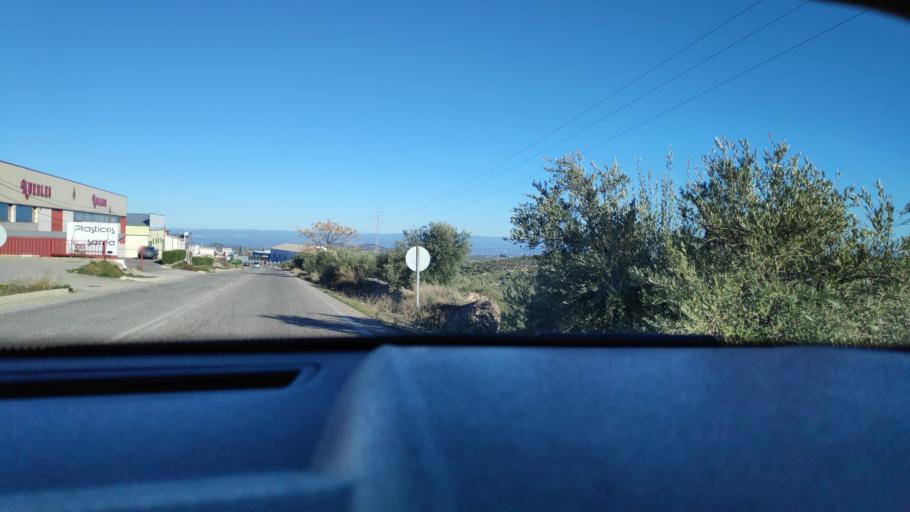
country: ES
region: Andalusia
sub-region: Provincia de Jaen
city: Mancha Real
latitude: 37.7947
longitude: -3.6072
